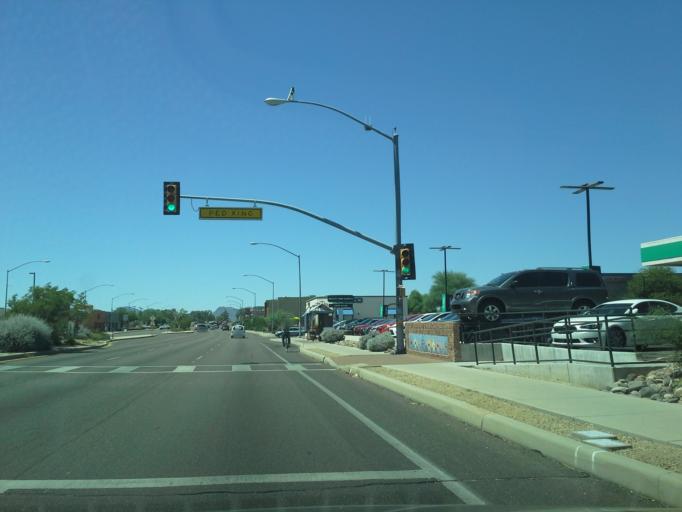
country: US
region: Arizona
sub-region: Pima County
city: Tucson
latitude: 32.2362
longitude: -110.9215
